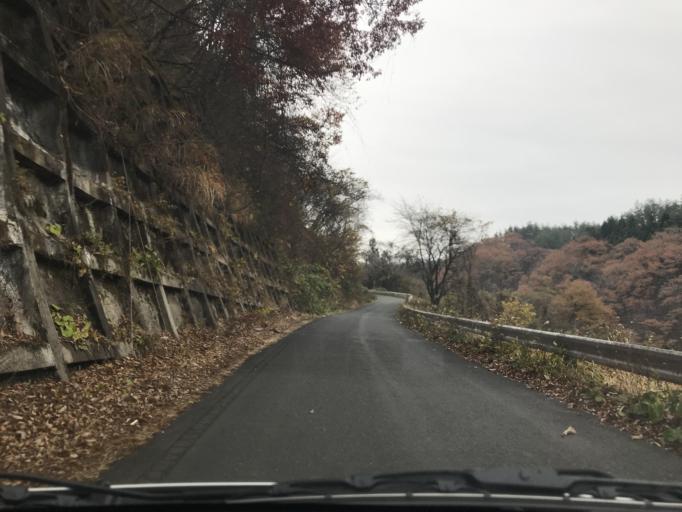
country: JP
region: Iwate
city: Ichinoseki
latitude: 39.0091
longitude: 141.0591
